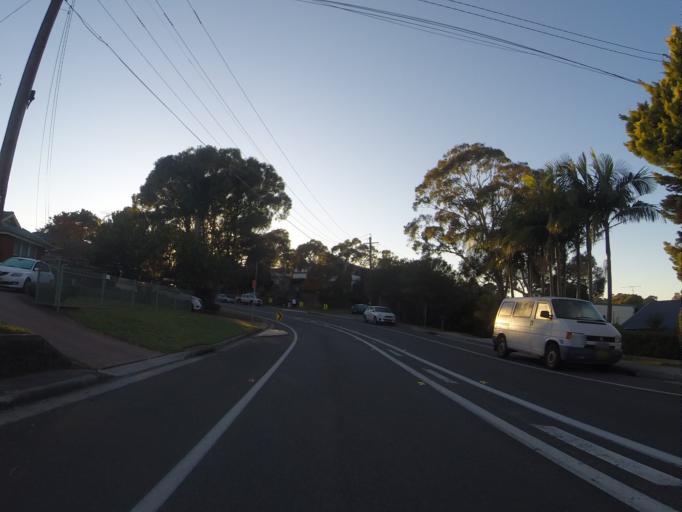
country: AU
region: New South Wales
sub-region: Sutherland Shire
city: Woronora Heights
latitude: -34.0470
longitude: 151.0152
